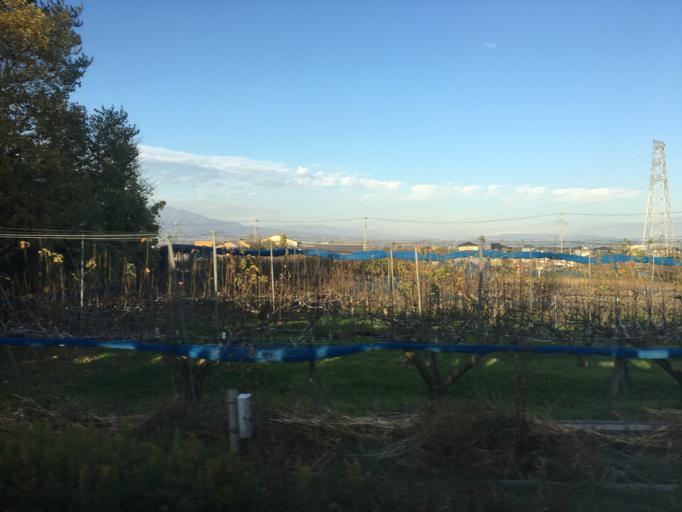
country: JP
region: Gunma
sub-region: Sawa-gun
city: Tamamura
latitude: 36.3631
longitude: 139.1231
